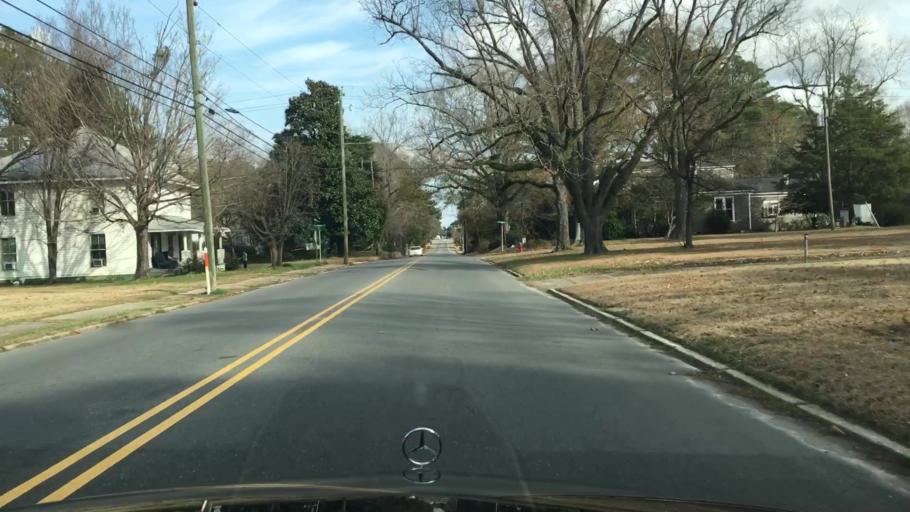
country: US
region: North Carolina
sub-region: Duplin County
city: Warsaw
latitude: 35.0003
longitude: -78.0879
